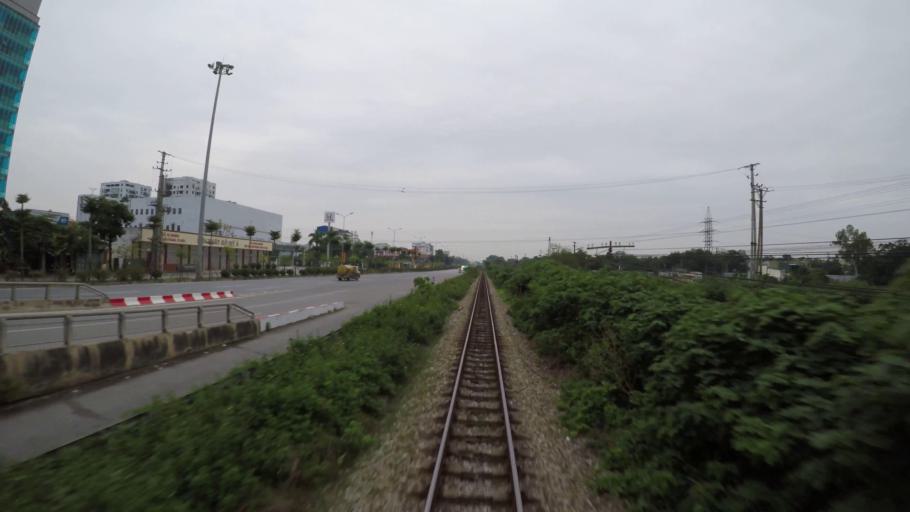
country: VN
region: Ha Noi
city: Trau Quy
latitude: 21.0062
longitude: 105.9587
